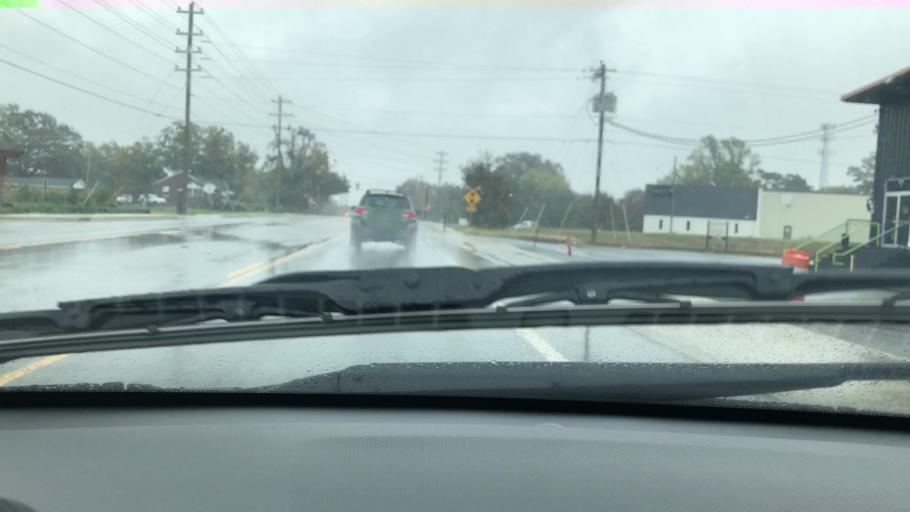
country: US
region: South Carolina
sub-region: Greenville County
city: Five Forks
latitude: 34.8362
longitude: -82.2758
